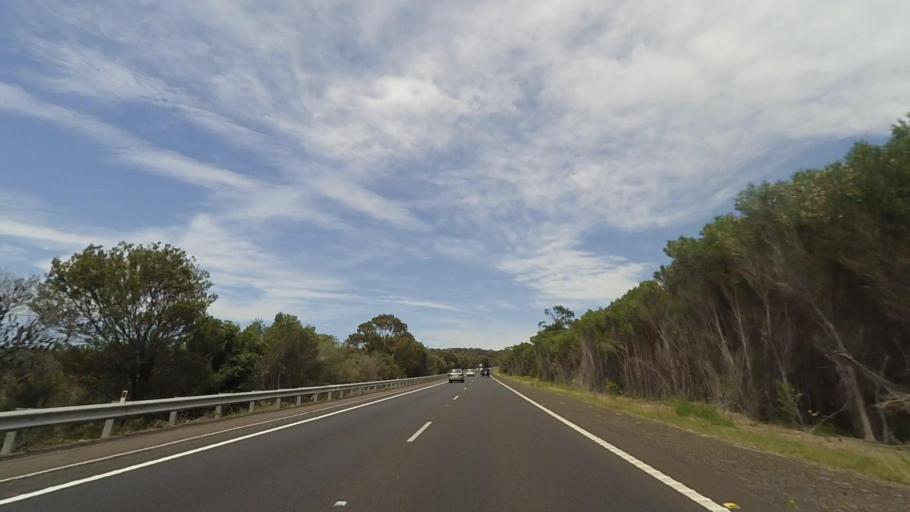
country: AU
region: New South Wales
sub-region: Wollongong
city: Helensburgh
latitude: -34.2346
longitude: 150.9469
